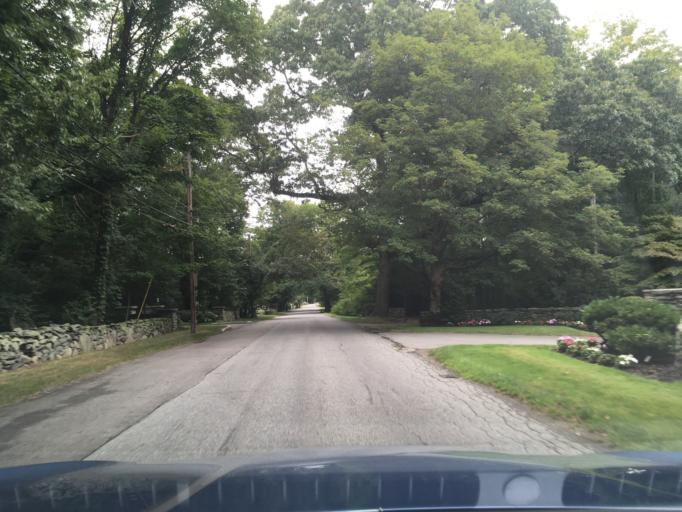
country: US
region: Rhode Island
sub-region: Bristol County
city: Barrington
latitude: 41.7197
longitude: -71.3028
